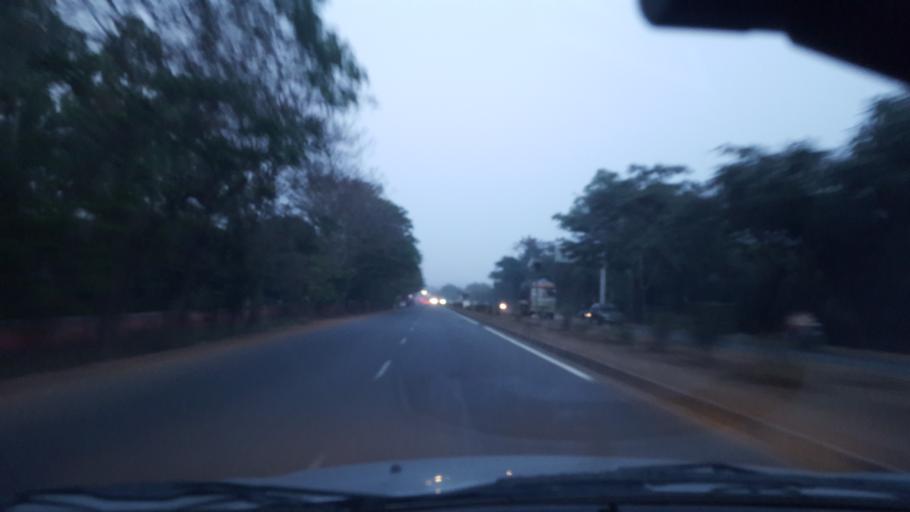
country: IN
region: Andhra Pradesh
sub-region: East Godavari
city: Rajahmundry
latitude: 17.0332
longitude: 81.8246
